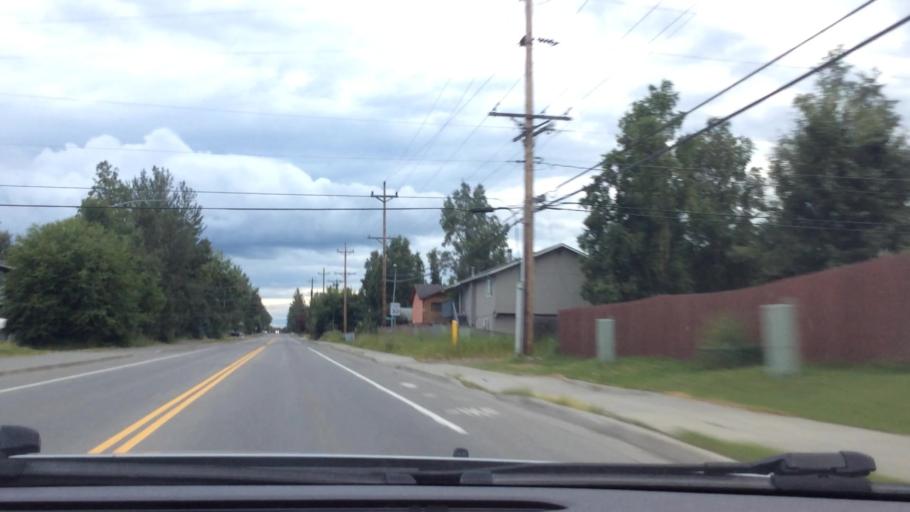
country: US
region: Alaska
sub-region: Anchorage Municipality
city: Elmendorf Air Force Base
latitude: 61.2131
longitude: -149.7559
